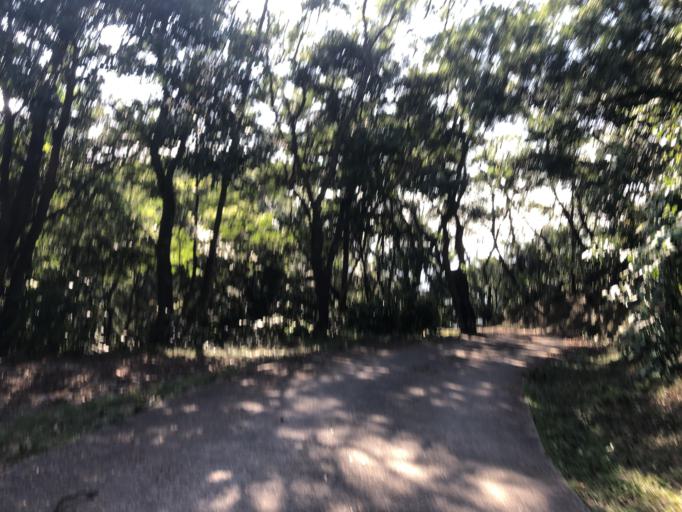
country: HK
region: Tsuen Wan
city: Tsuen Wan
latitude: 22.3932
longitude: 114.0859
